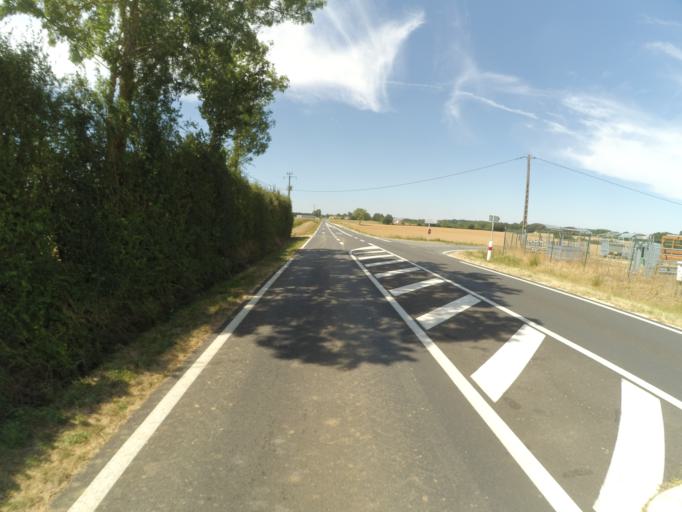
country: FR
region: Poitou-Charentes
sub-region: Departement de la Vienne
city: Saint-Maurice-la-Clouere
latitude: 46.3657
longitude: 0.4254
